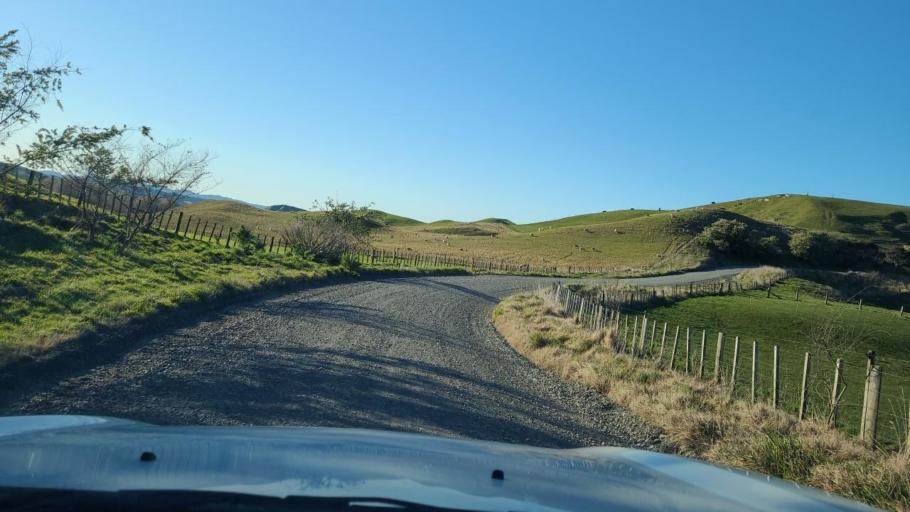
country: NZ
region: Hawke's Bay
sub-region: Napier City
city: Taradale
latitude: -39.4022
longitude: 176.5617
